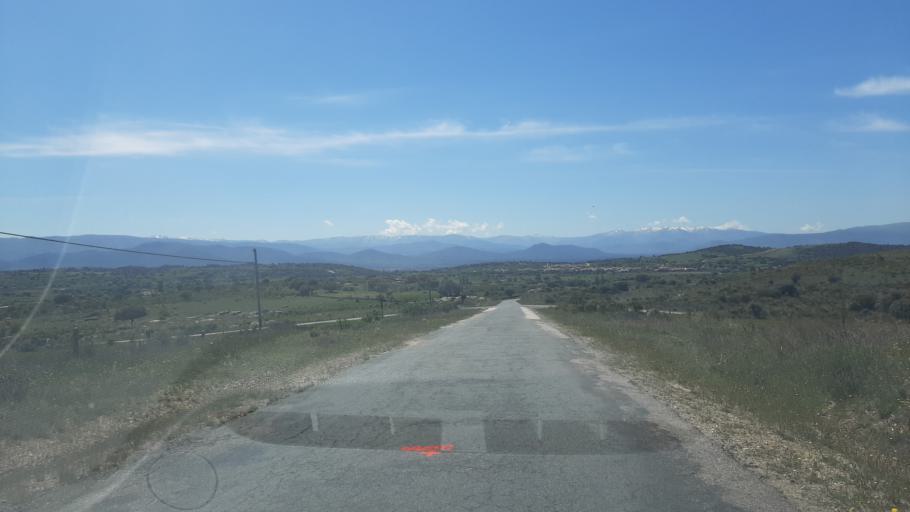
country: ES
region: Castille and Leon
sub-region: Provincia de Avila
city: Narrillos del Alamo
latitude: 40.5573
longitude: -5.4404
